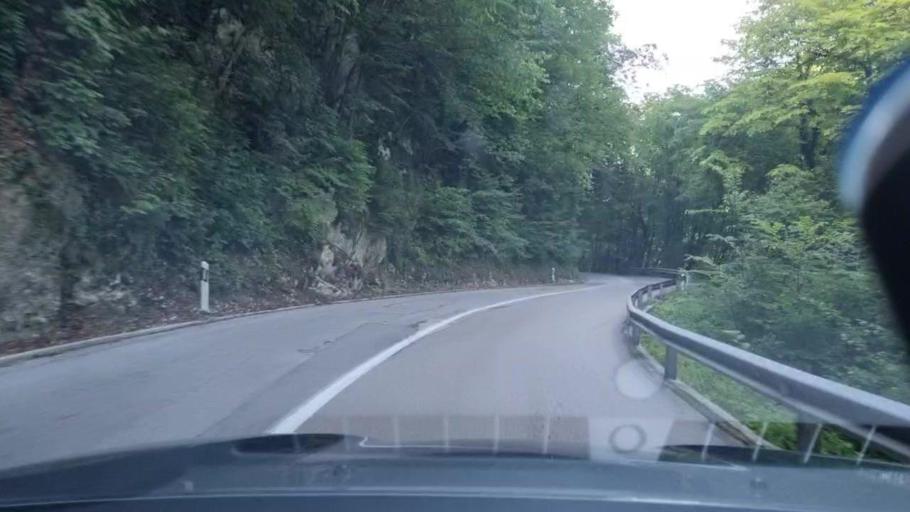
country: BA
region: Federation of Bosnia and Herzegovina
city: Stijena
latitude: 44.8891
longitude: 16.0542
